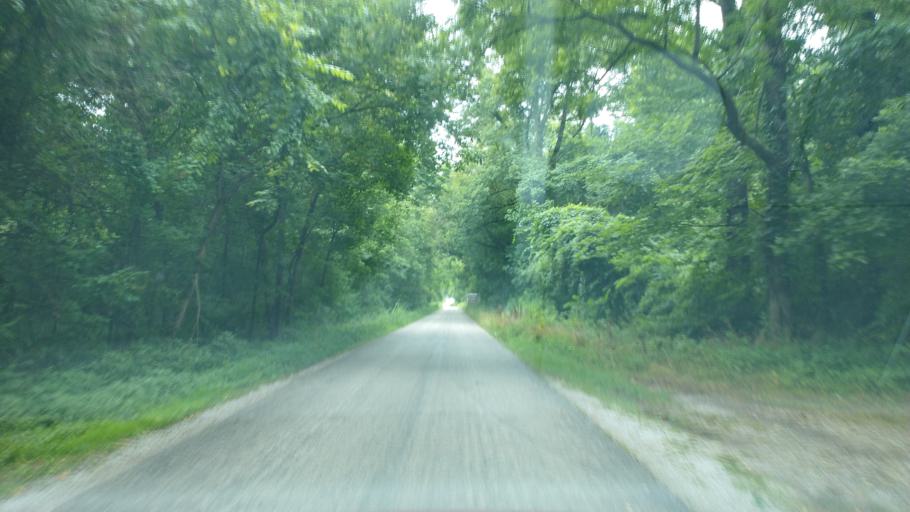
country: US
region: Ohio
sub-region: Meigs County
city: Middleport
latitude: 38.9334
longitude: -82.0794
